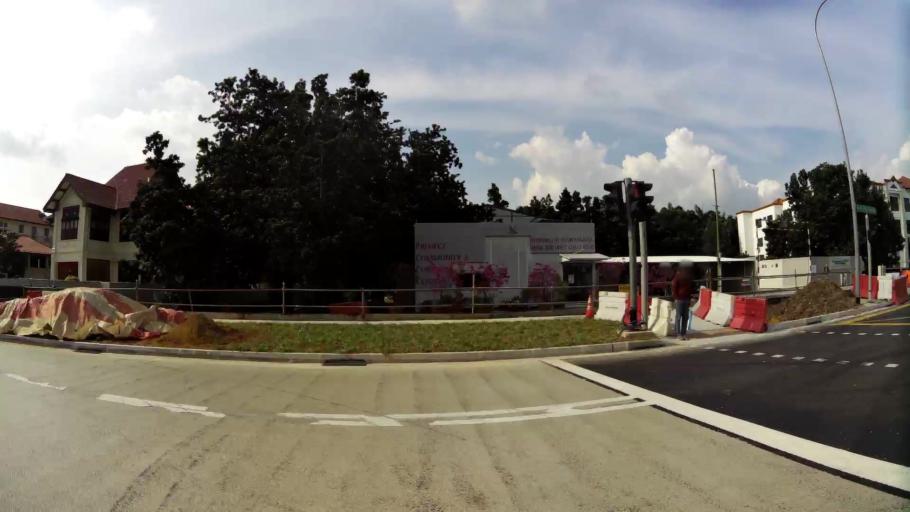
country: SG
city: Singapore
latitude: 1.2906
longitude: 103.7735
